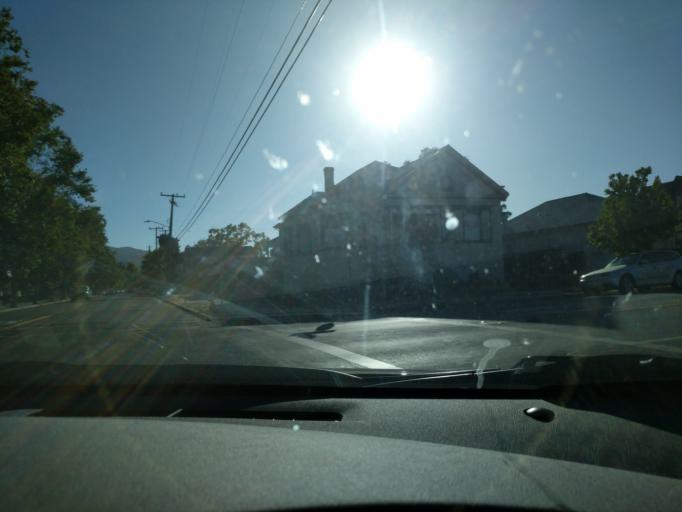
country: US
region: California
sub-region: Santa Clara County
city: Gilroy
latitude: 37.0062
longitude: -121.5710
